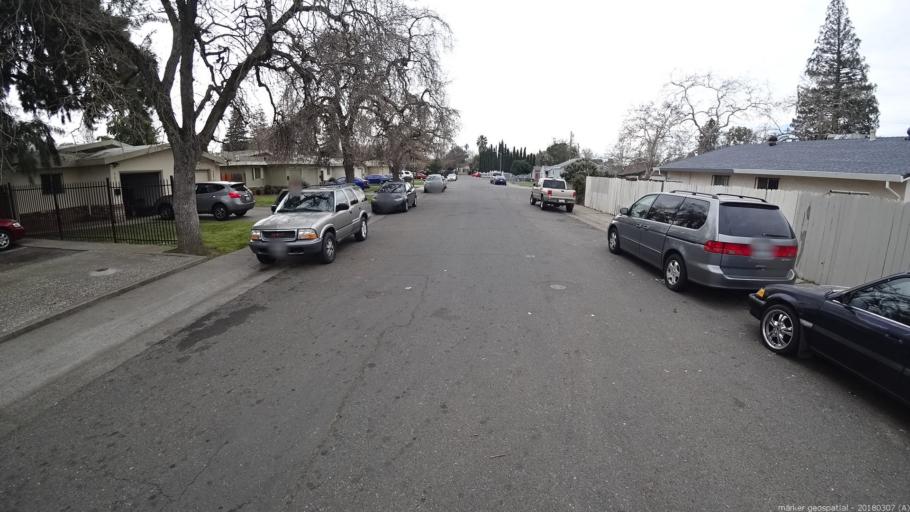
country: US
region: California
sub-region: Sacramento County
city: Parkway
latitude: 38.5335
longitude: -121.4617
